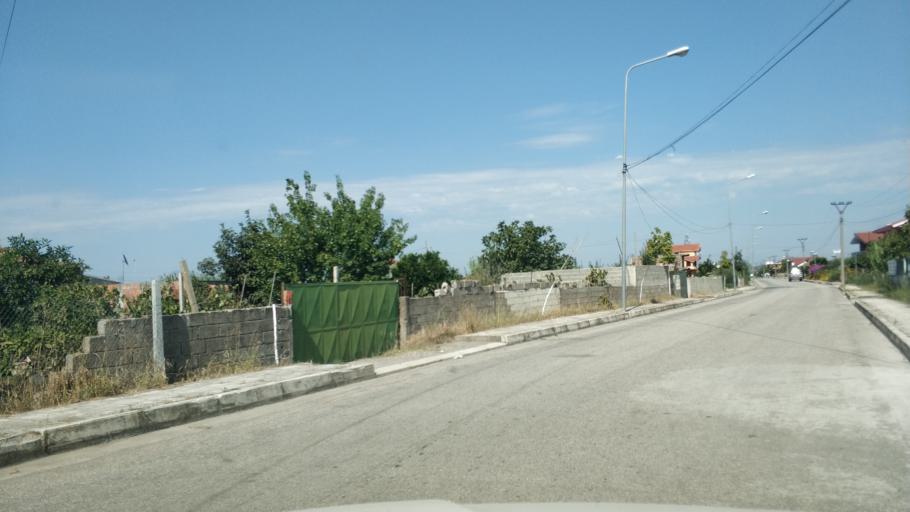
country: AL
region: Fier
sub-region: Rrethi i Lushnjes
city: Divjake
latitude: 40.9989
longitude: 19.5254
